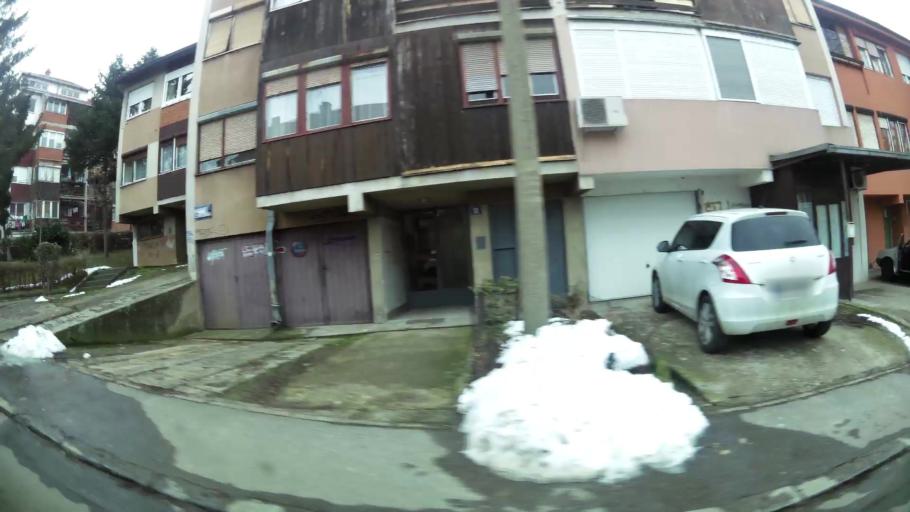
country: RS
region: Central Serbia
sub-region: Belgrade
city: Cukarica
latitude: 44.7629
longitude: 20.4090
